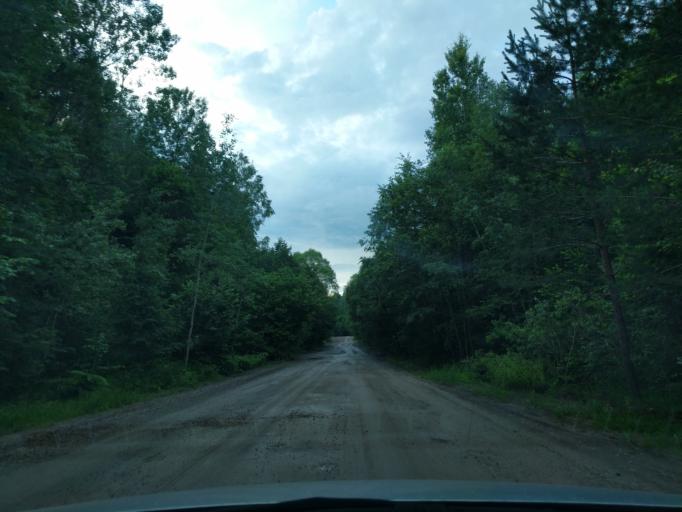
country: RU
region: Kaluga
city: Myatlevo
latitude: 54.8443
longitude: 35.6184
